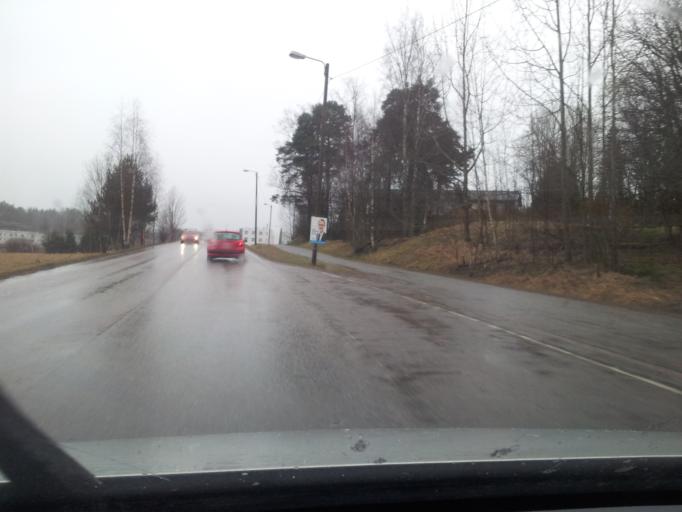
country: FI
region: Uusimaa
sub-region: Helsinki
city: Kirkkonummi
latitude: 60.1666
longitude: 24.5410
